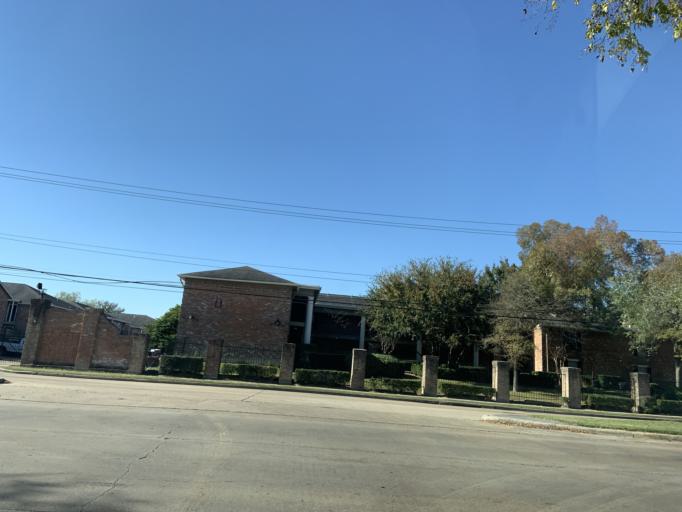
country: US
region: Texas
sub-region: Harris County
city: Bellaire
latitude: 29.6816
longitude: -95.5086
